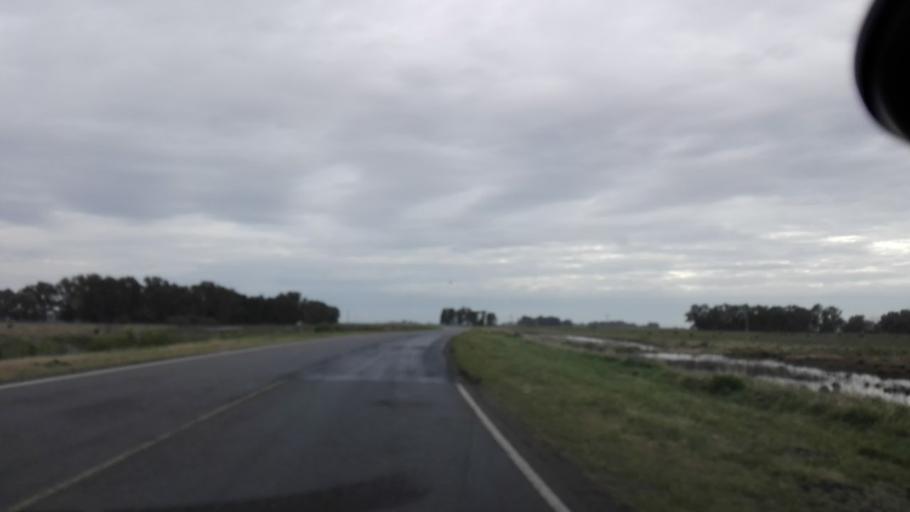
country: AR
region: Buenos Aires
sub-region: Partido de Rauch
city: Rauch
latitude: -36.6065
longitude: -59.0591
